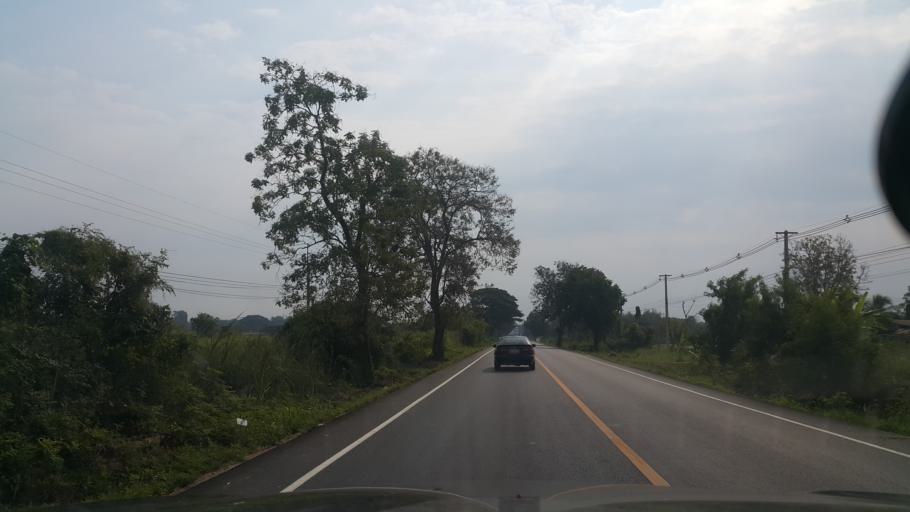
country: TH
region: Sukhothai
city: Si Samrong
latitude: 17.1782
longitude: 99.8444
